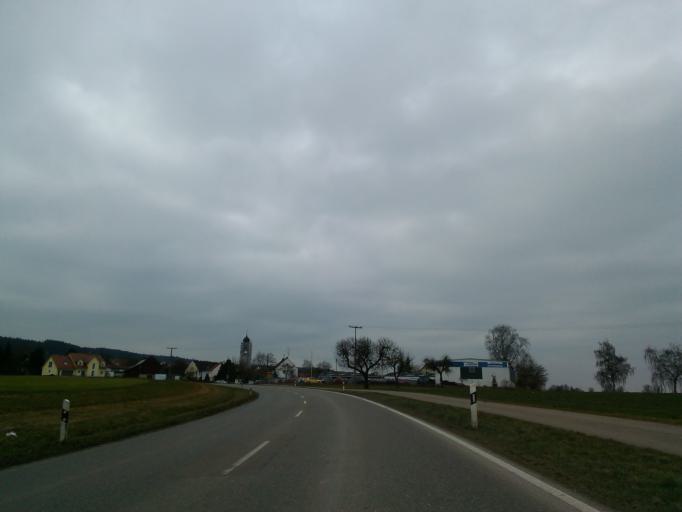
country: DE
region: Bavaria
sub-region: Swabia
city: Ustersbach
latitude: 48.3099
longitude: 10.6179
